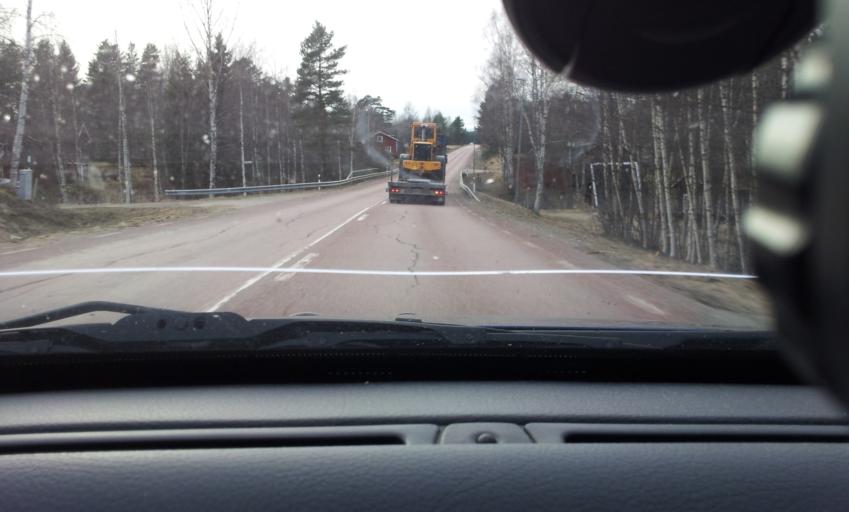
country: SE
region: Gaevleborg
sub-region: Ljusdals Kommun
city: Farila
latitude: 61.8003
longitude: 15.8003
